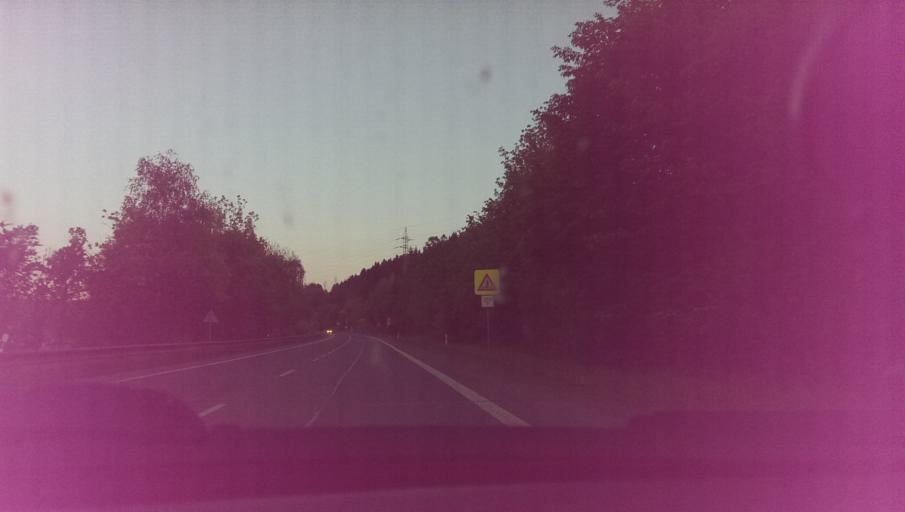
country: CZ
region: Zlin
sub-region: Okres Vsetin
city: Vsetin
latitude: 49.3437
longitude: 17.9724
